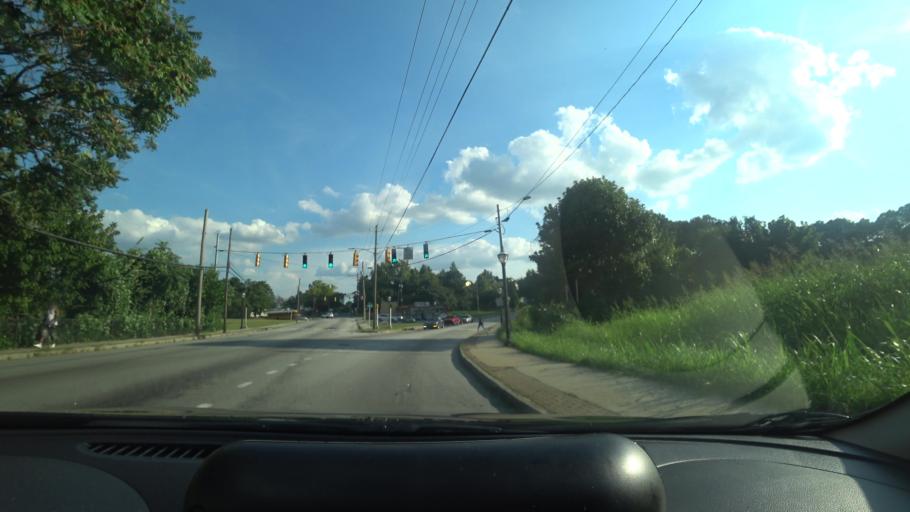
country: US
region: Georgia
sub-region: Fulton County
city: Atlanta
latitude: 33.7099
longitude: -84.3935
